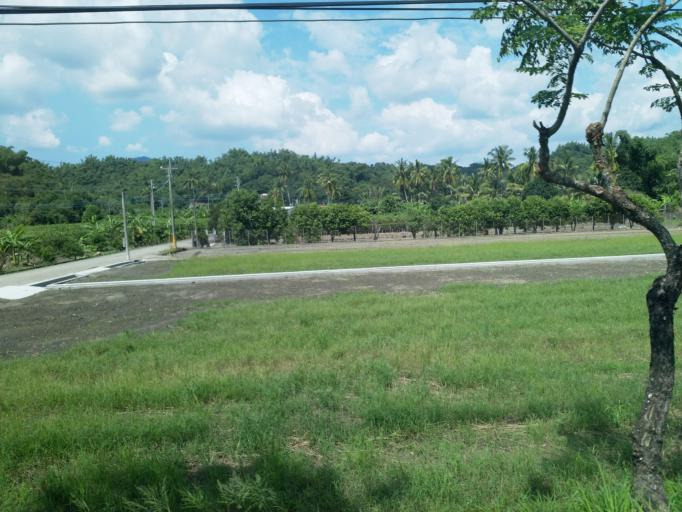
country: TW
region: Taiwan
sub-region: Pingtung
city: Pingtung
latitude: 22.8801
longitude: 120.5661
